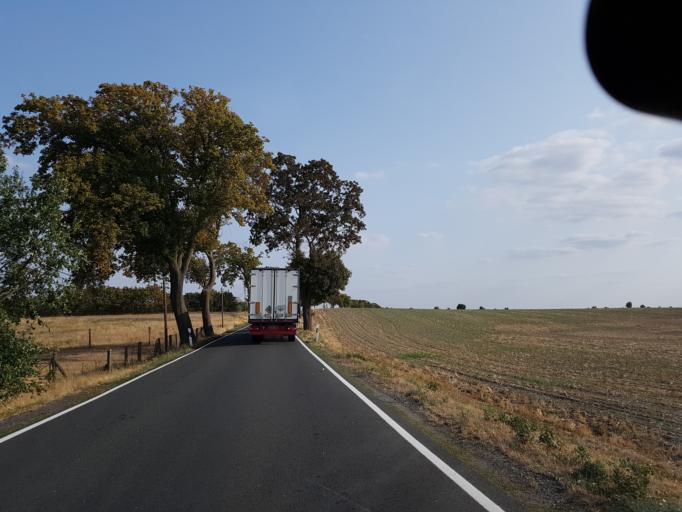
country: DE
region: Saxony-Anhalt
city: Pretzsch
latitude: 51.7011
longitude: 12.8196
